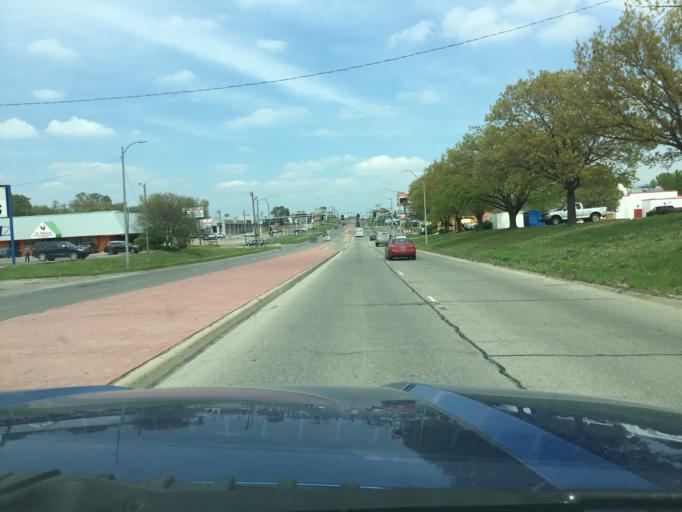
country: US
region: Kansas
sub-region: Shawnee County
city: Topeka
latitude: 39.0034
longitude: -95.6876
